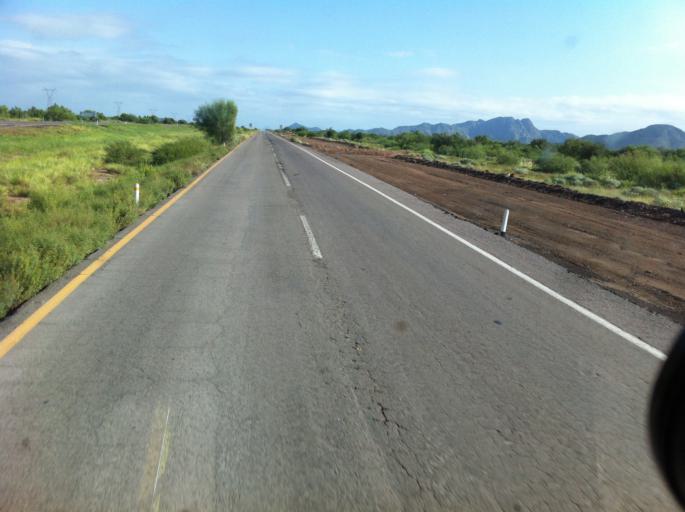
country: MX
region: Sonora
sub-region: Hermosillo
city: Miguel Aleman (La Doce)
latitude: 28.5320
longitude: -111.0453
